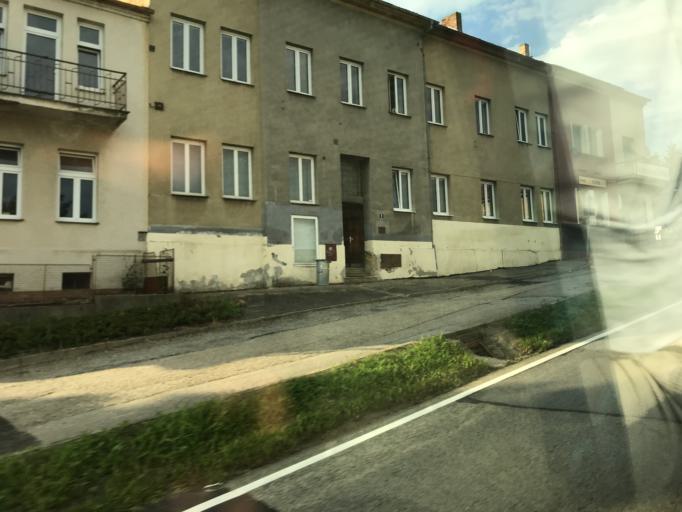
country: CZ
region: Jihocesky
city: Rudolfov
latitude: 48.9930
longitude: 14.5371
